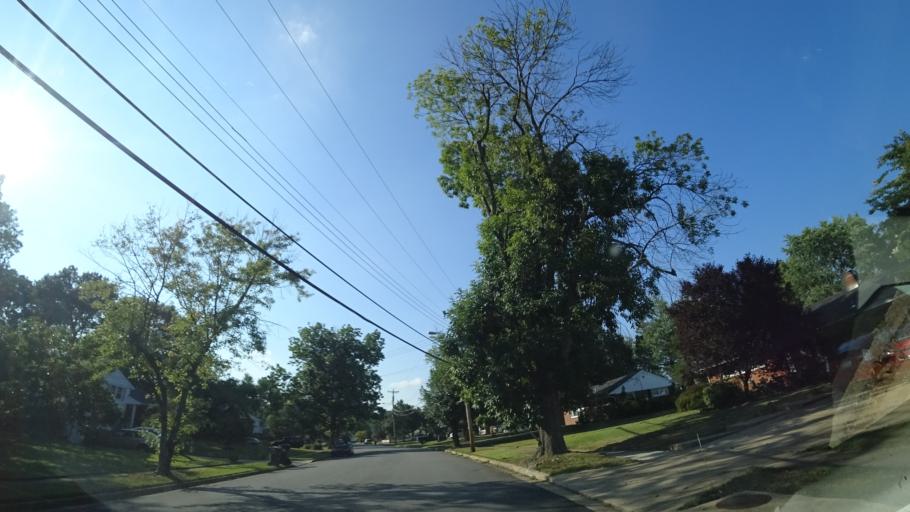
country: US
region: Virginia
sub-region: Fairfax County
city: Springfield
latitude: 38.8090
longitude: -77.1763
